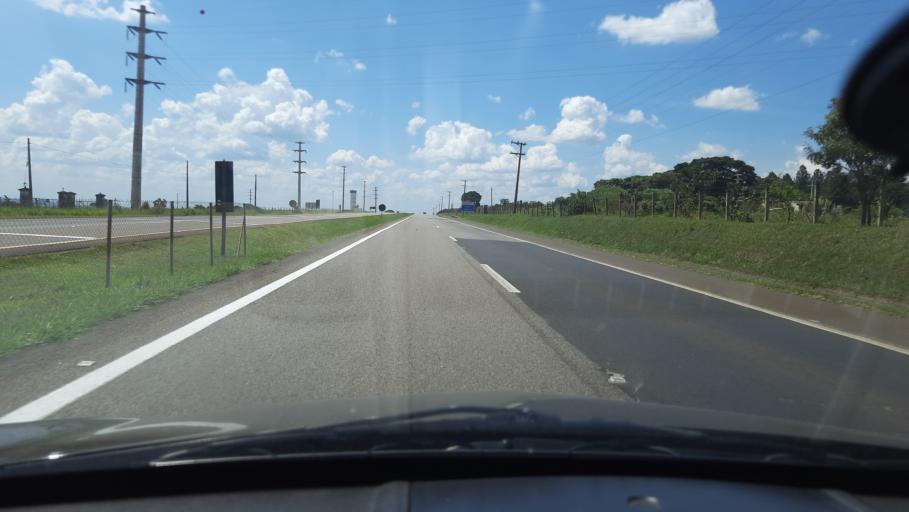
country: BR
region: Sao Paulo
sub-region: Casa Branca
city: Casa Branca
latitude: -21.7629
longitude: -47.0699
